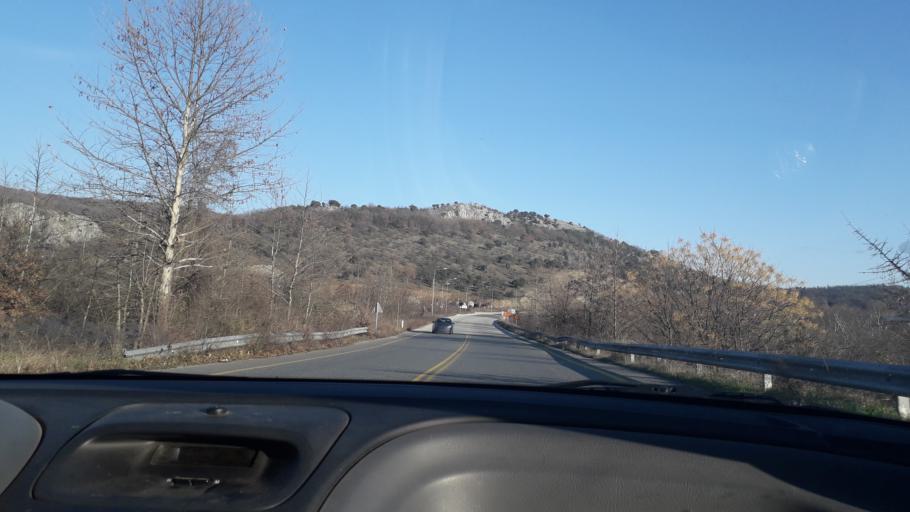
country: GR
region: Central Macedonia
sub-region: Nomos Pellis
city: Profitis Ilias
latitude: 40.8419
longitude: 22.1103
